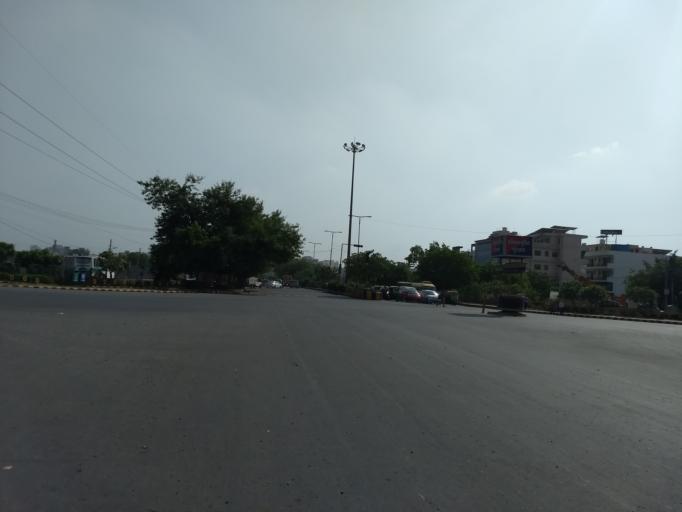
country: IN
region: Haryana
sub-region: Gurgaon
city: Gurgaon
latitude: 28.4348
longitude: 77.0495
